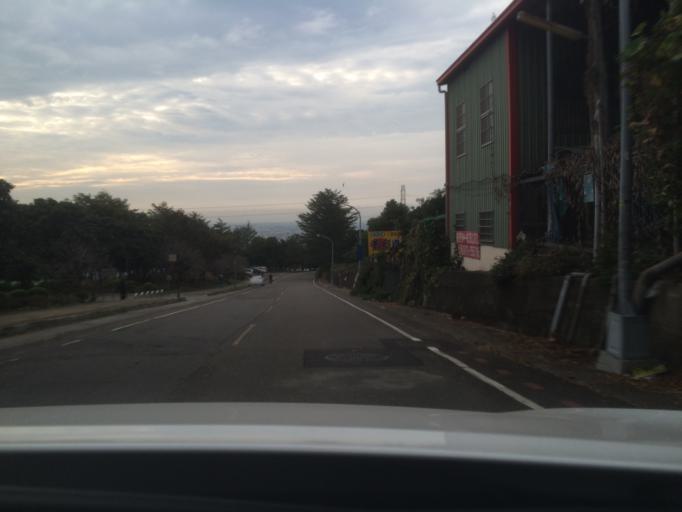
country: TW
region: Taiwan
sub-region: Nantou
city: Nantou
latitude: 23.9404
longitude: 120.6222
